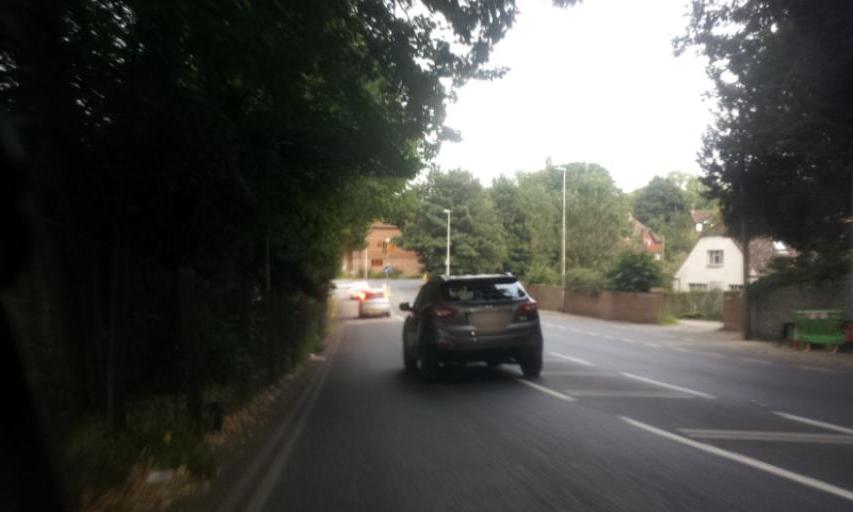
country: GB
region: England
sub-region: Kent
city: Gillingham
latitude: 51.3644
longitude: 0.5533
